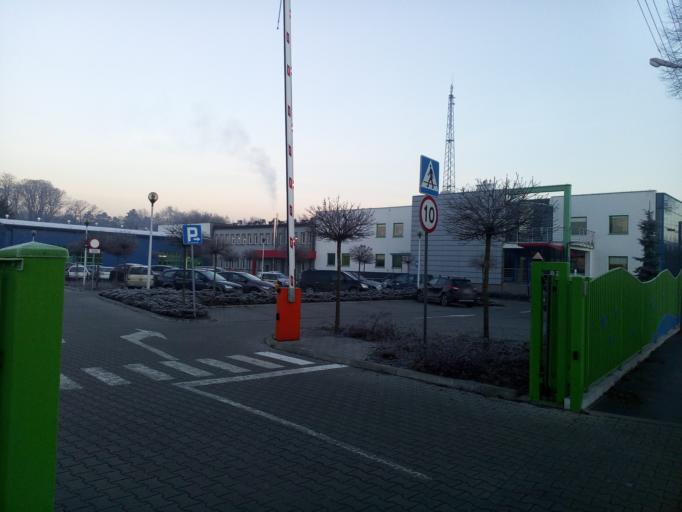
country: PL
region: Lesser Poland Voivodeship
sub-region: Powiat nowosadecki
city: Nowy Sacz
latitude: 49.6163
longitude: 20.6889
